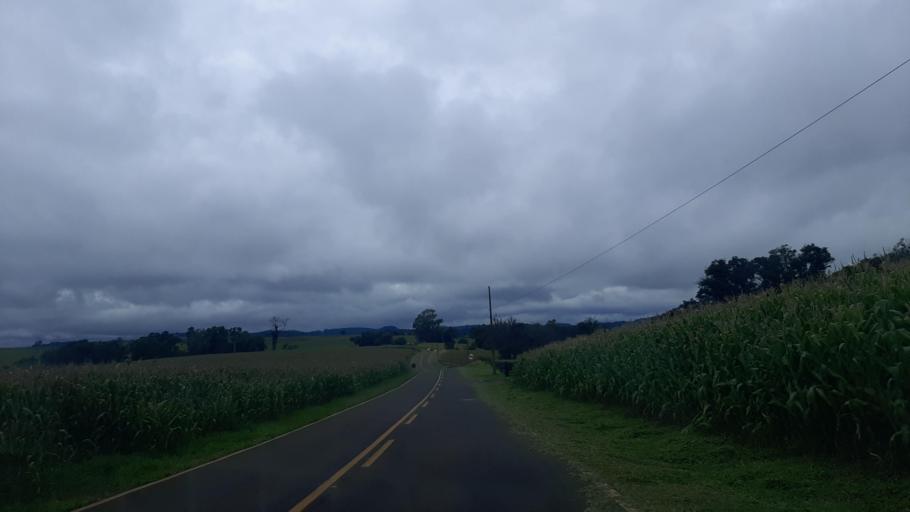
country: BR
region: Parana
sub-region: Ampere
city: Ampere
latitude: -25.9594
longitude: -53.4467
